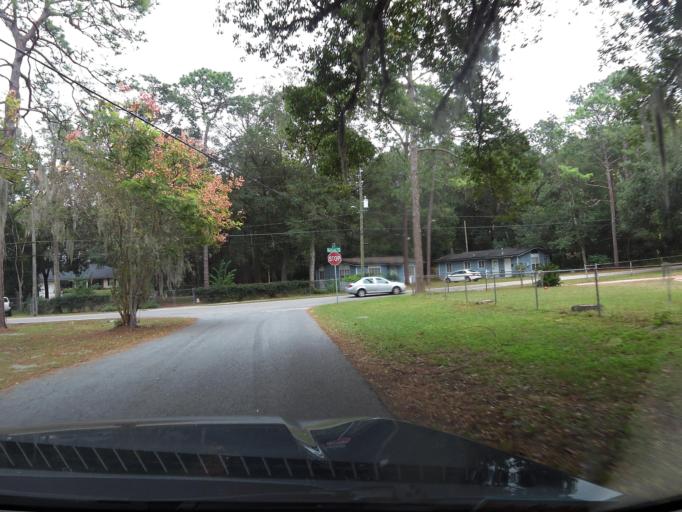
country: US
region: Florida
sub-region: Duval County
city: Jacksonville
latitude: 30.3064
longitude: -81.6033
